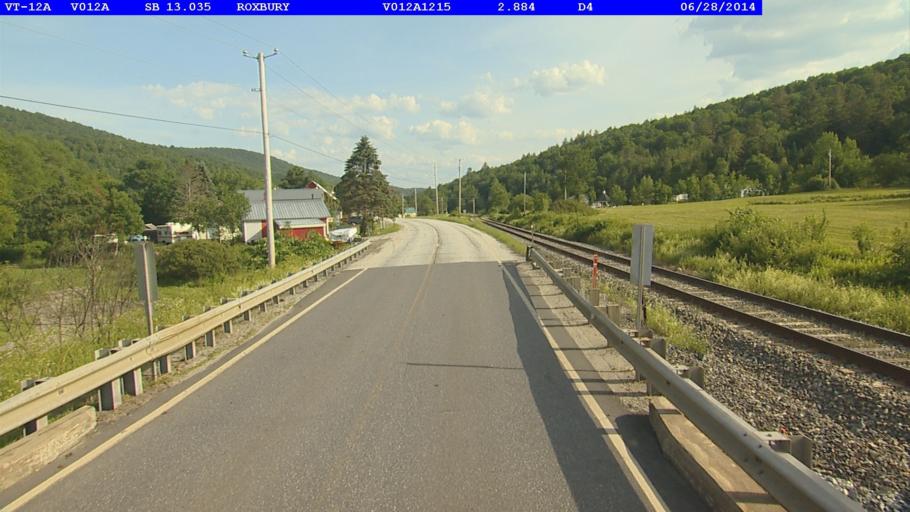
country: US
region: Vermont
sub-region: Washington County
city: Northfield
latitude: 44.0698
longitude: -72.7457
